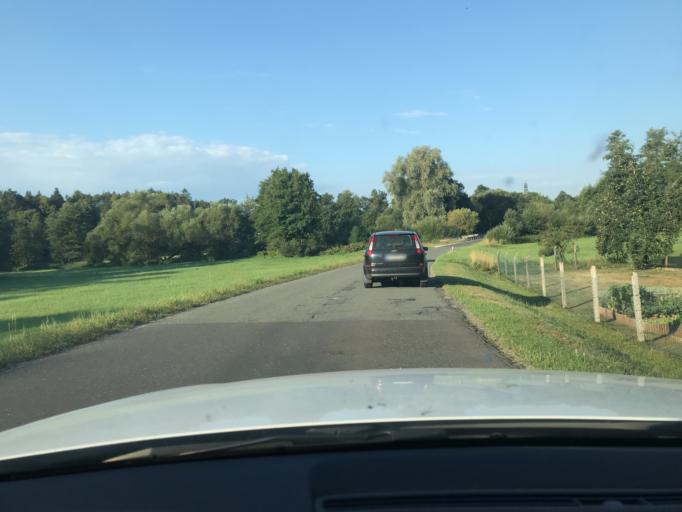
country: DE
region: Bavaria
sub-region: Upper Palatinate
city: Auerbach
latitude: 49.7074
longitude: 11.5943
